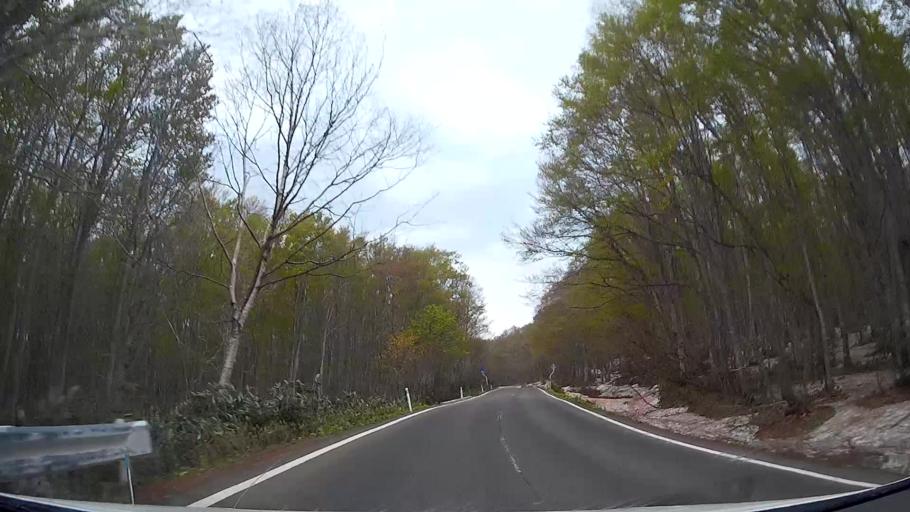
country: JP
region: Aomori
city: Aomori Shi
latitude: 40.6857
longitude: 140.8342
